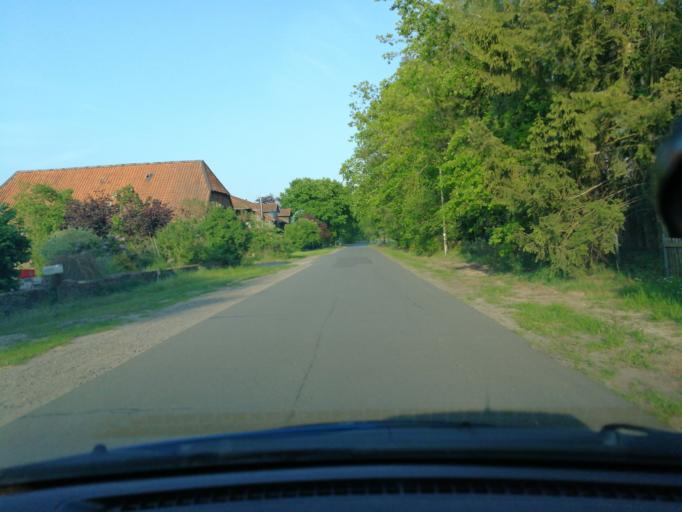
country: DE
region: Lower Saxony
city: Rullstorf
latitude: 53.2898
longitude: 10.5610
